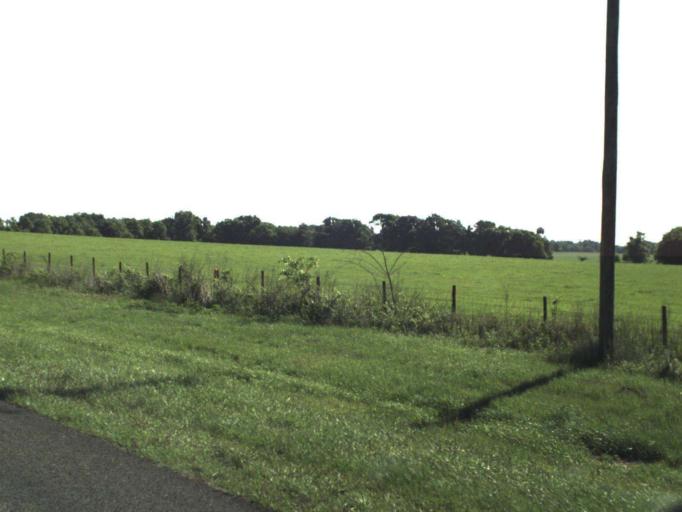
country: US
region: Florida
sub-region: Marion County
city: Citra
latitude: 29.3400
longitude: -82.1511
